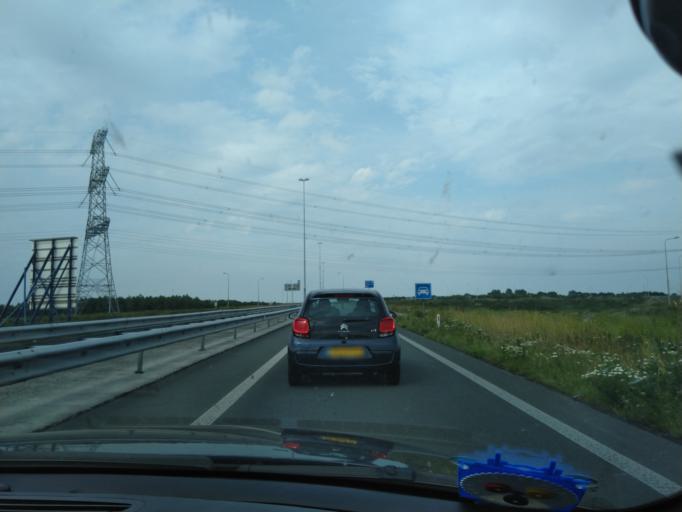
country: NL
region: Drenthe
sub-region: Gemeente Coevorden
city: Dalen
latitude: 52.7254
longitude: 6.7848
